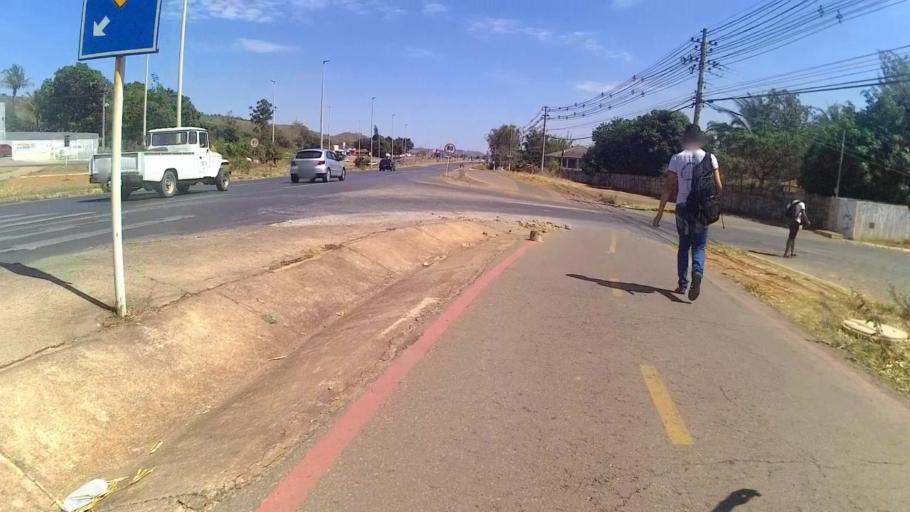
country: BR
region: Federal District
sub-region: Brasilia
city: Brasilia
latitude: -15.6612
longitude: -47.8438
